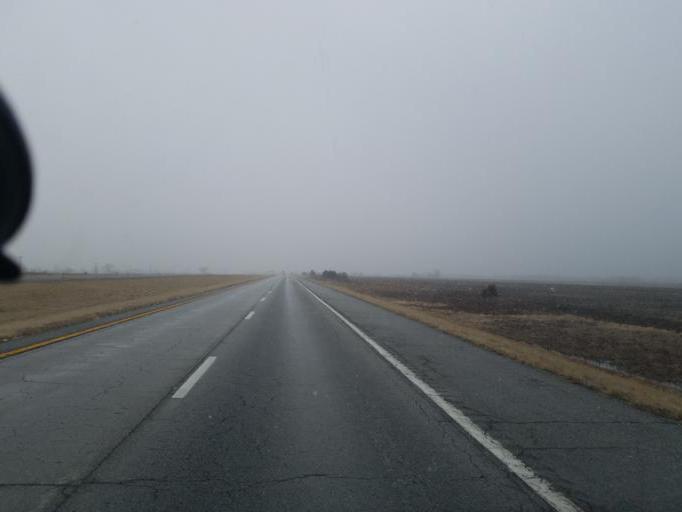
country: US
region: Missouri
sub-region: Macon County
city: La Plata
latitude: 39.9449
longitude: -92.4772
